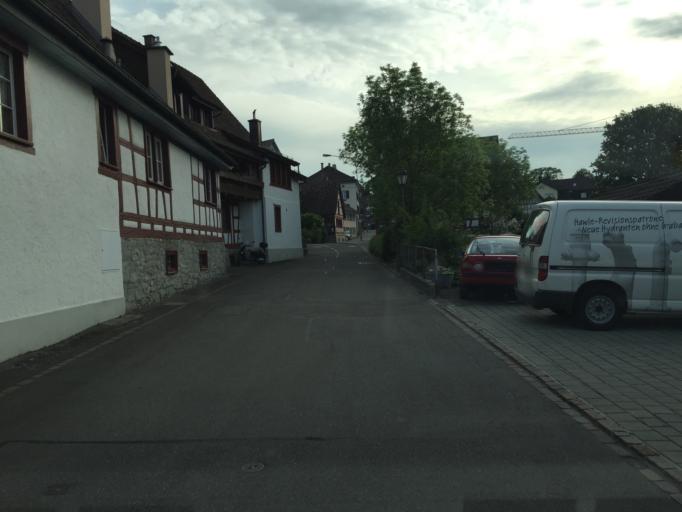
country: CH
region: Thurgau
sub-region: Kreuzlingen District
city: Ermatingen
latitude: 47.6697
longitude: 9.0788
